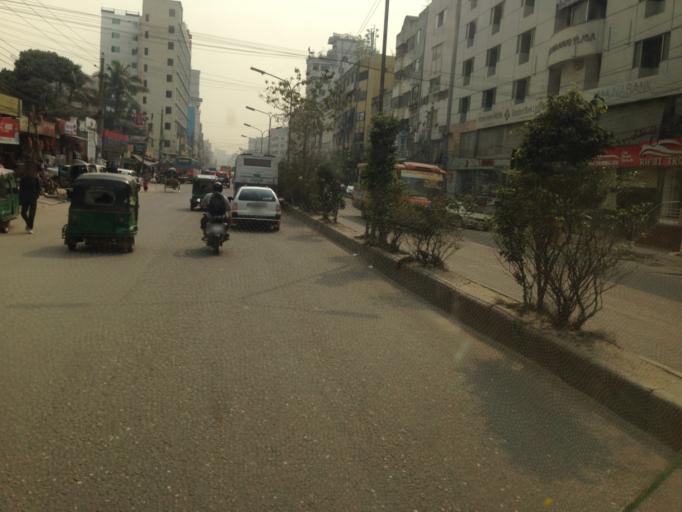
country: BD
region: Dhaka
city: Tungi
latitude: 23.8175
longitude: 90.4211
